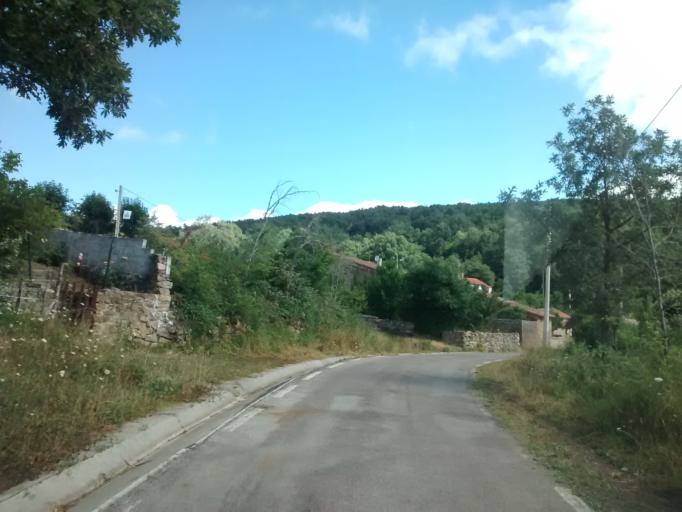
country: ES
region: Castille and Leon
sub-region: Provincia de Palencia
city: Berzosilla
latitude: 42.8794
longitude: -4.0531
